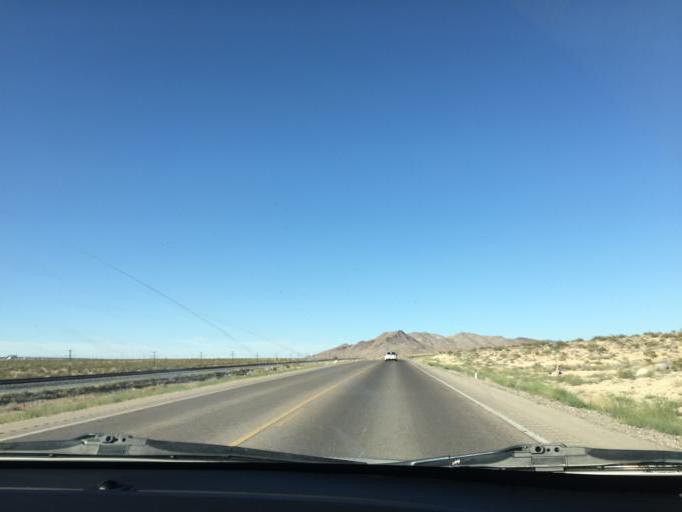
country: US
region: Nevada
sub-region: Clark County
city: Enterprise
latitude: 35.8662
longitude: -115.2443
